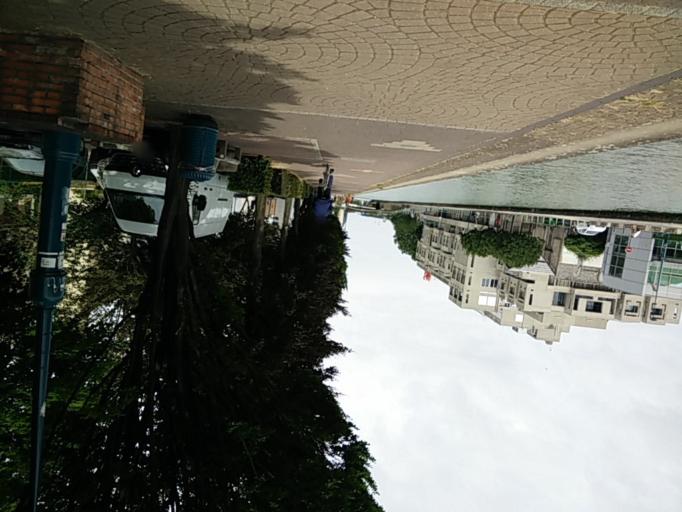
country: FR
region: Ile-de-France
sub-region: Departement de Seine-Saint-Denis
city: Pantin
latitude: 48.8957
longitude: 2.4044
